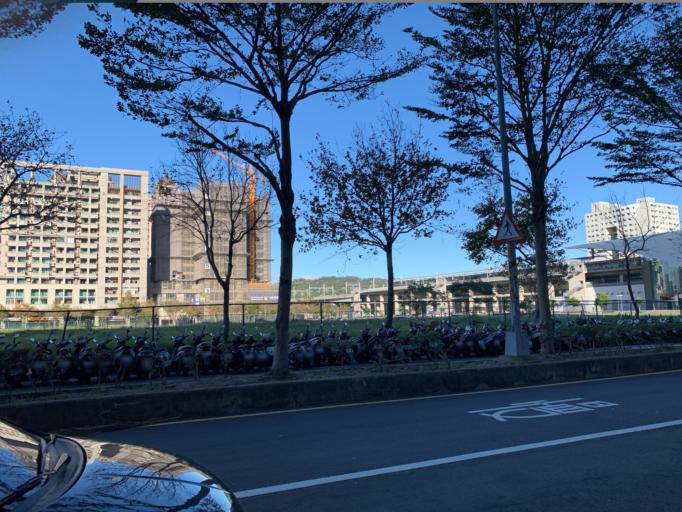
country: TW
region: Taiwan
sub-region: Hsinchu
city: Zhubei
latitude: 24.8078
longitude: 121.0381
